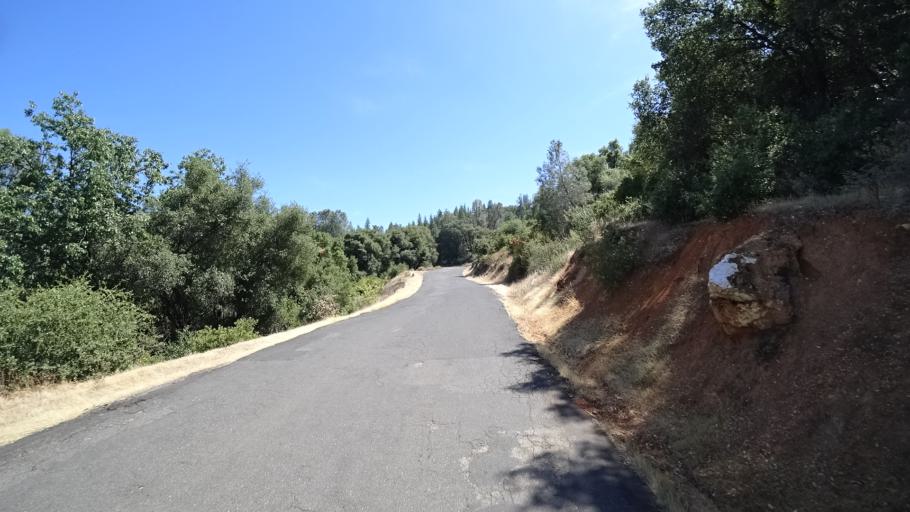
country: US
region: California
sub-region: Calaveras County
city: Murphys
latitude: 38.1498
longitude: -120.4739
